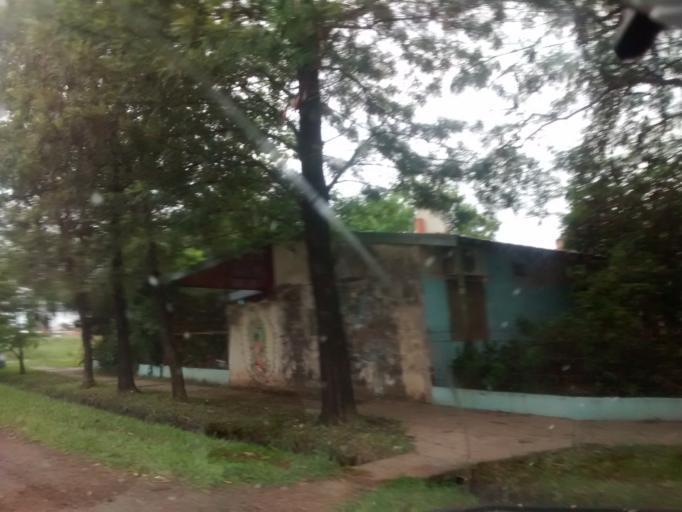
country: AR
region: Chaco
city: Fontana
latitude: -27.4531
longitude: -59.0234
